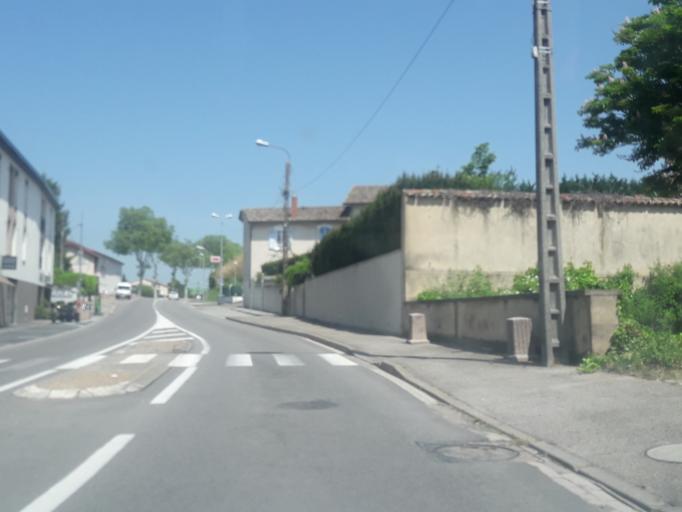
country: FR
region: Rhone-Alpes
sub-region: Departement de l'Ain
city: Mionnay
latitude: 45.8954
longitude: 4.9312
